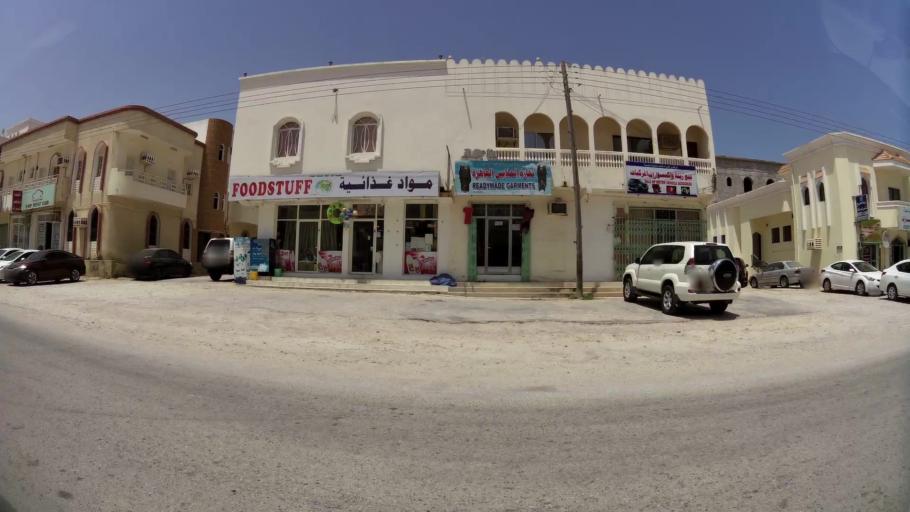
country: OM
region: Zufar
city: Salalah
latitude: 17.0133
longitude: 54.0792
